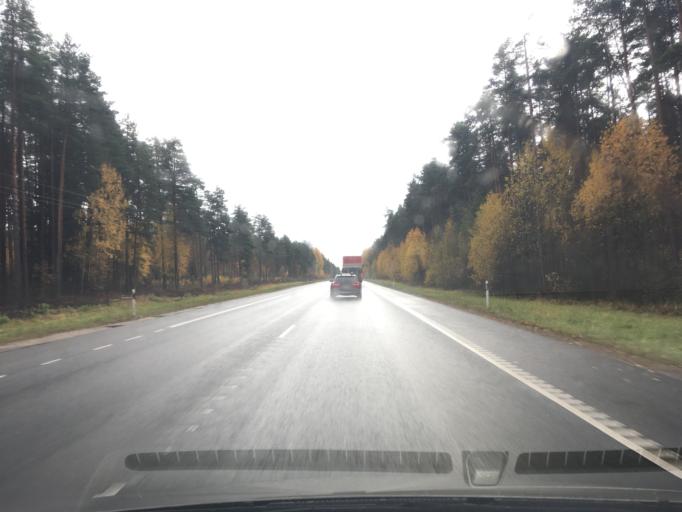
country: EE
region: Tartu
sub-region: Tartu linn
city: Tartu
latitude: 58.3964
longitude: 26.6611
